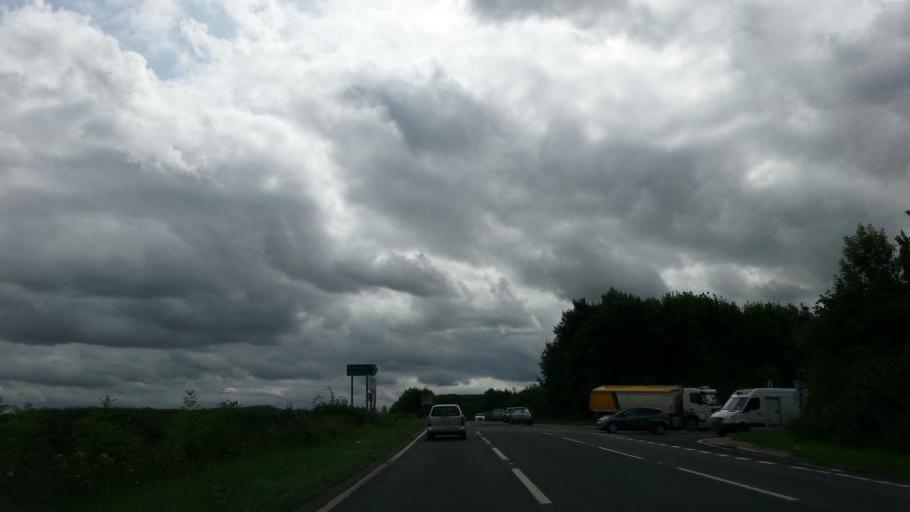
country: GB
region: England
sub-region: Northamptonshire
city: Brixworth
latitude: 52.4020
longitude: -0.9174
